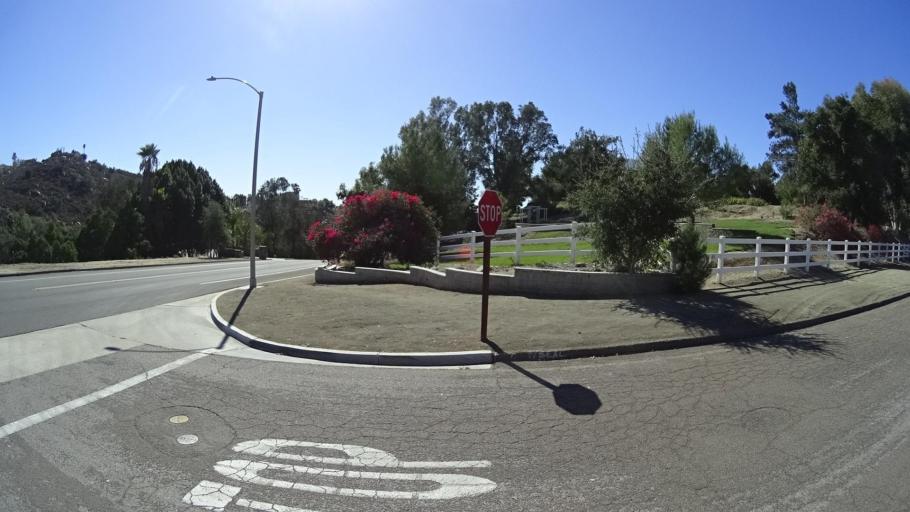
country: US
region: California
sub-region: San Diego County
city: Lakeside
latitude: 32.8651
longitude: -116.8687
